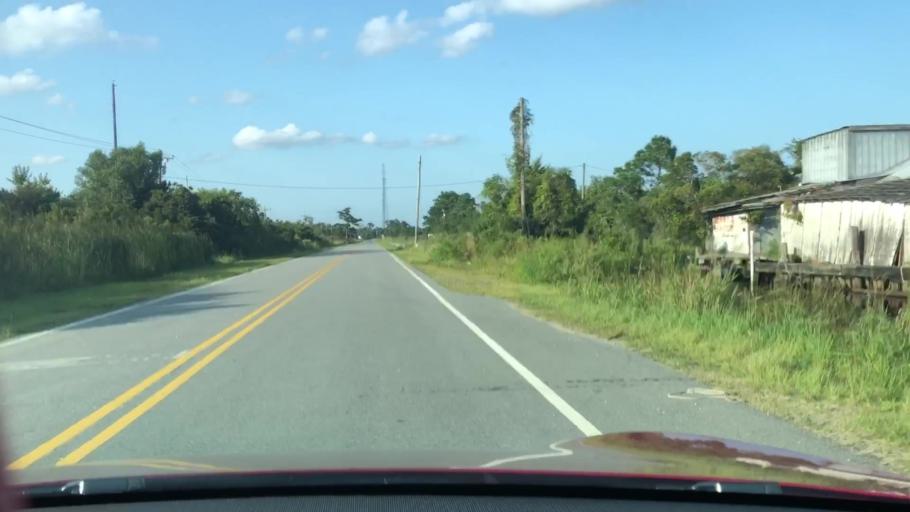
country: US
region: North Carolina
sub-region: Dare County
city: Wanchese
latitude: 35.6984
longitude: -75.7726
